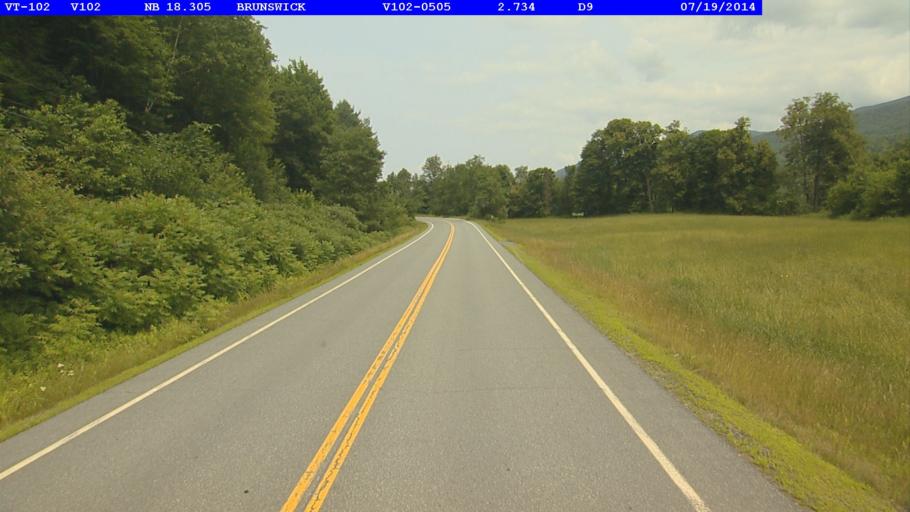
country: US
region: New Hampshire
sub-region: Coos County
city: Stratford
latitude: 44.6985
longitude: -71.6029
